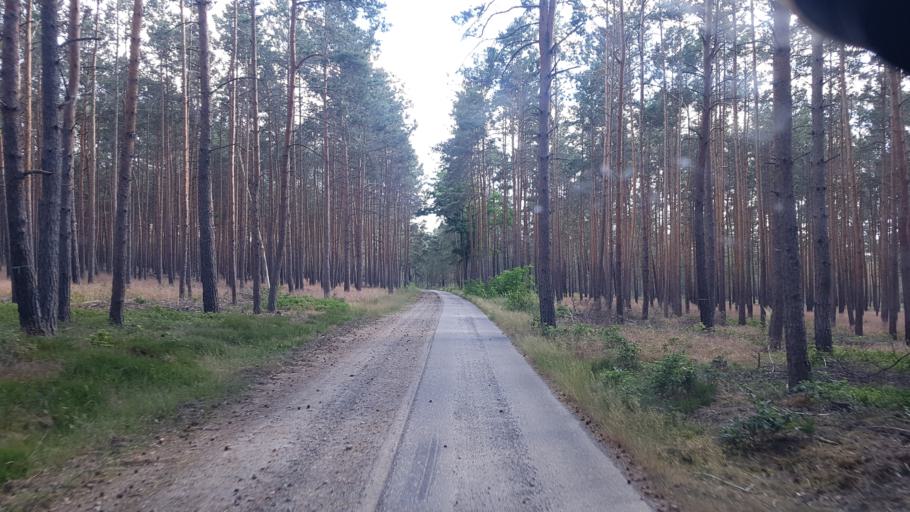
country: DE
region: Brandenburg
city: Trobitz
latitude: 51.6304
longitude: 13.4364
